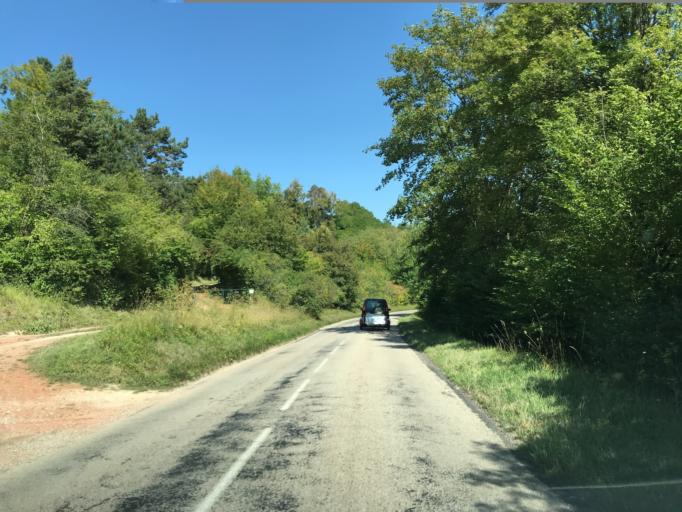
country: FR
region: Haute-Normandie
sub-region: Departement de l'Eure
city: Heudreville-sur-Eure
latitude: 49.1073
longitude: 1.2073
